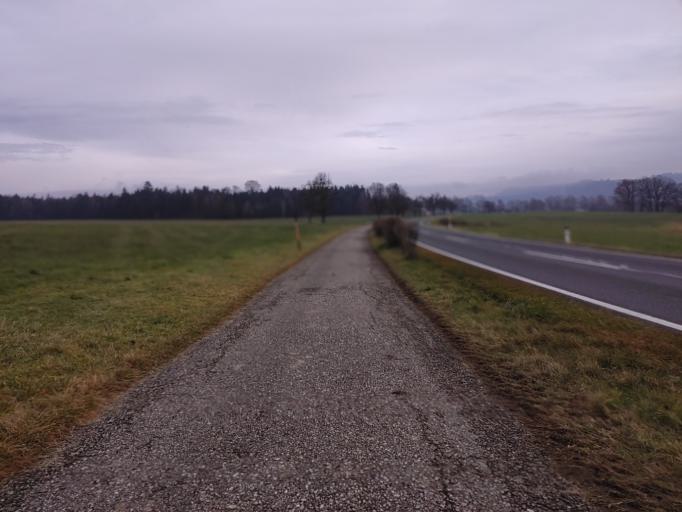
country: AT
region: Salzburg
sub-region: Politischer Bezirk Salzburg-Umgebung
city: Mattsee
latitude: 47.9839
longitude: 13.0945
